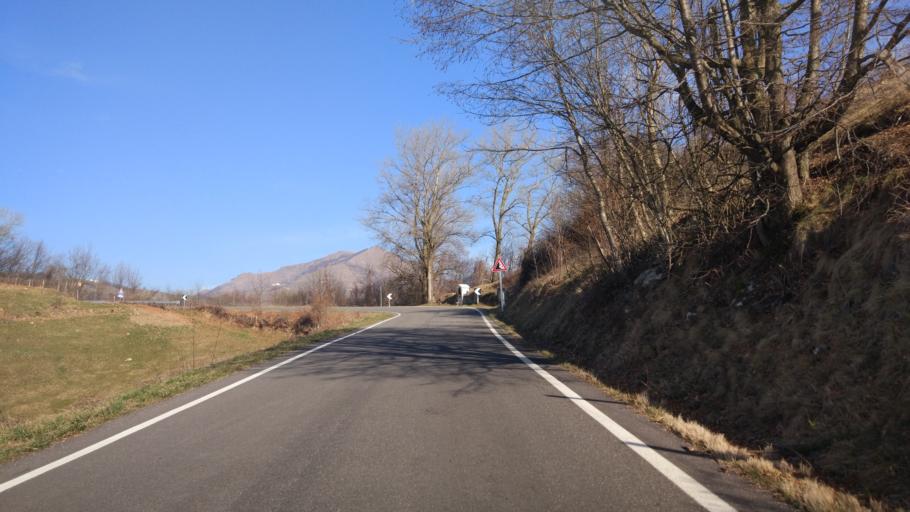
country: IT
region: Veneto
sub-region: Provincia di Verona
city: Selva di Progno
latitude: 45.6124
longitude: 11.1797
